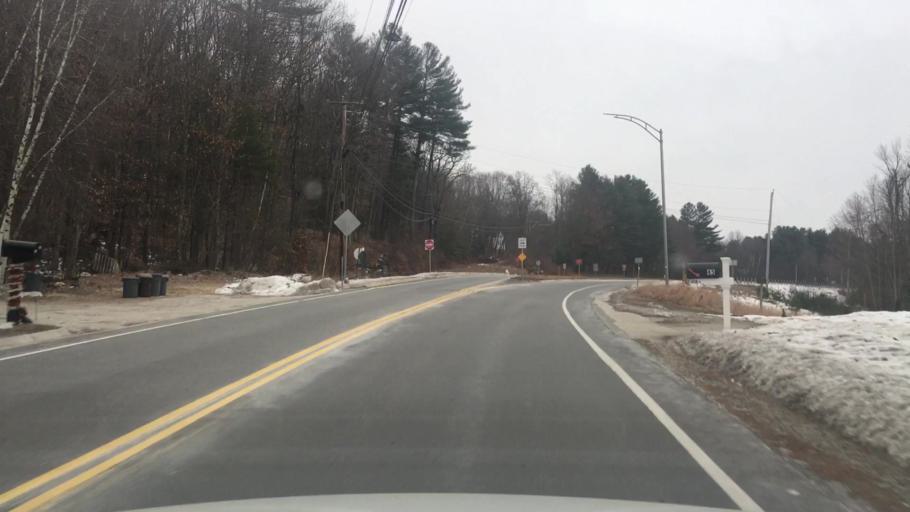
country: US
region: New Hampshire
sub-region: Merrimack County
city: Hopkinton
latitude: 43.1887
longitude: -71.6625
